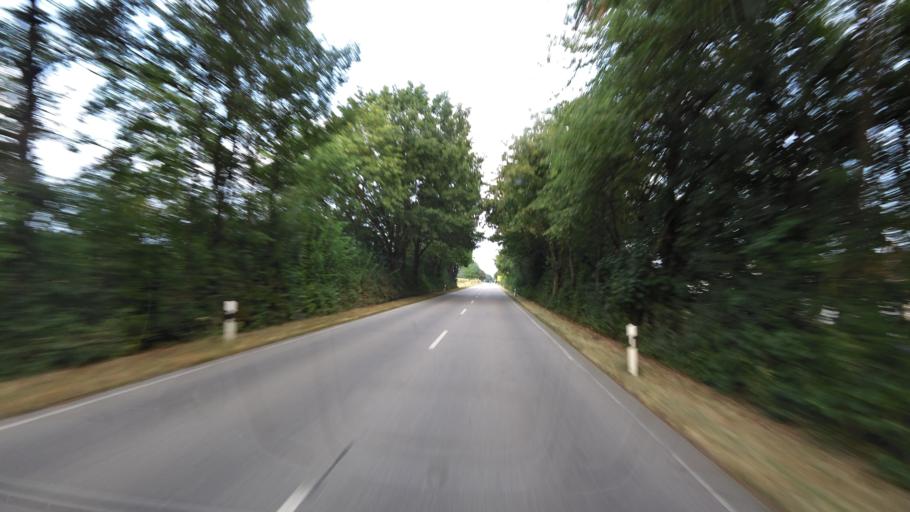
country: DE
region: Bavaria
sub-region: Lower Bavaria
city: Kirchham
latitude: 48.3508
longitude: 13.2643
